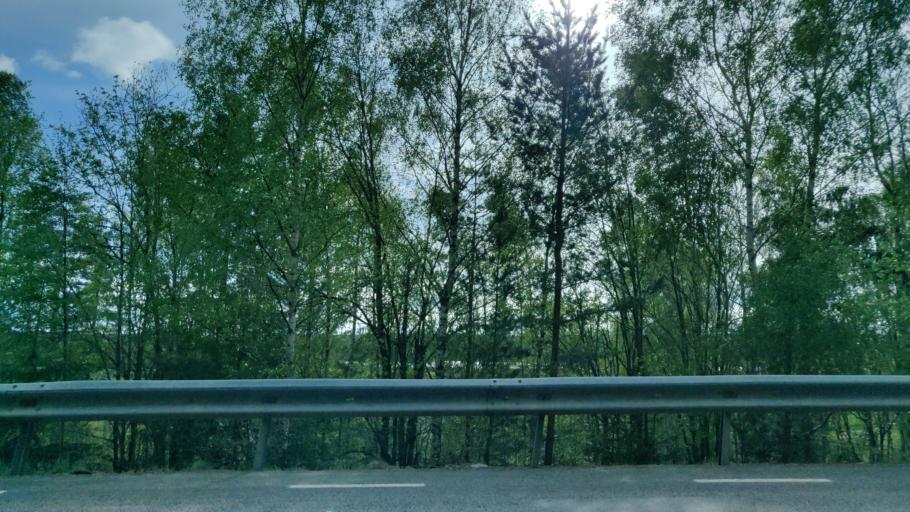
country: SE
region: Vaermland
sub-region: Forshaga Kommun
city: Deje
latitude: 59.5908
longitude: 13.4563
